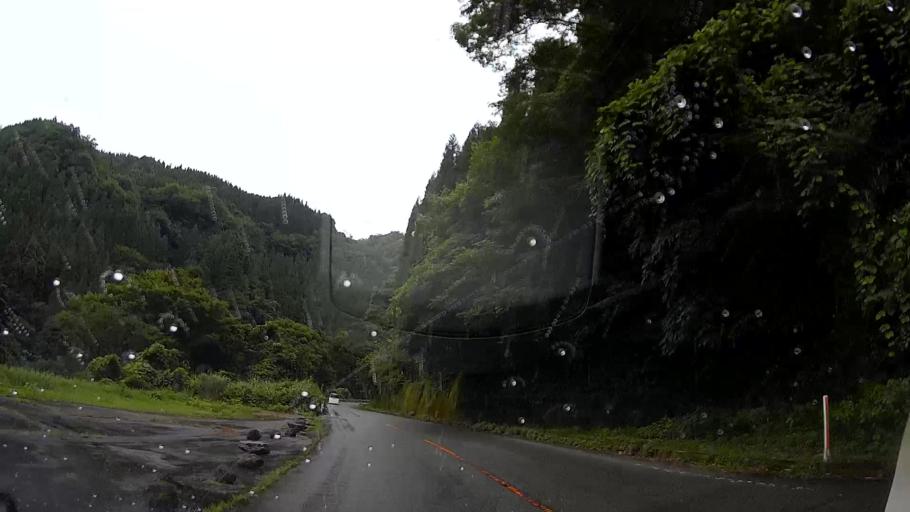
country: JP
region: Oita
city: Tsukawaki
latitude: 33.1692
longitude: 131.0401
